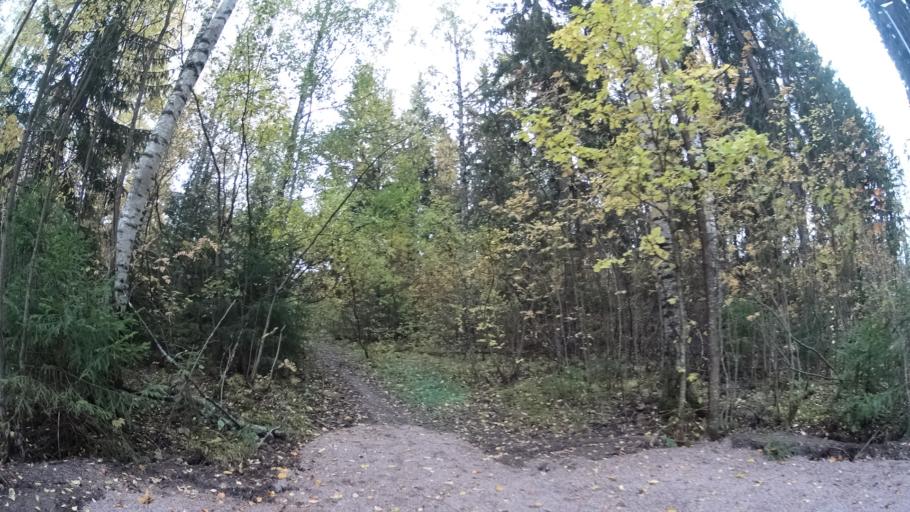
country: FI
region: Uusimaa
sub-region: Helsinki
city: Espoo
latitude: 60.2308
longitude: 24.6461
